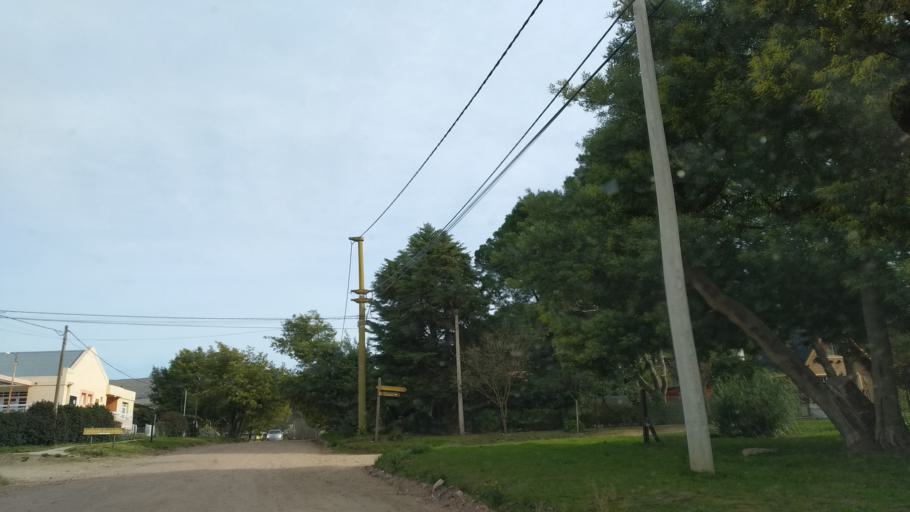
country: AR
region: Buenos Aires
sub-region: Partido de Tornquist
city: Tornquist
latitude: -38.0859
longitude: -61.9310
